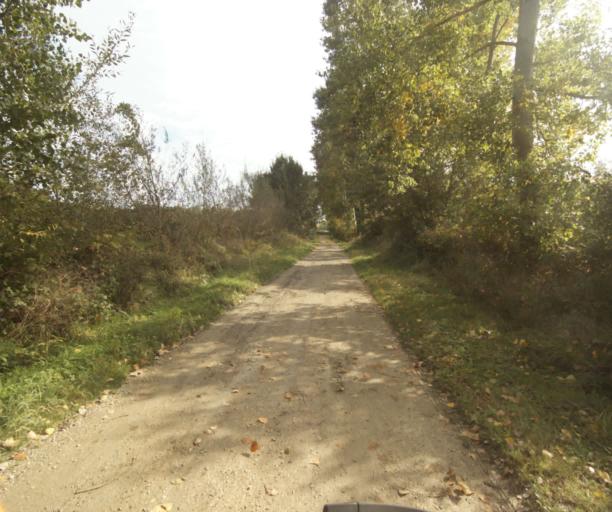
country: FR
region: Midi-Pyrenees
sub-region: Departement du Tarn-et-Garonne
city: Finhan
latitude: 43.9134
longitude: 1.1991
